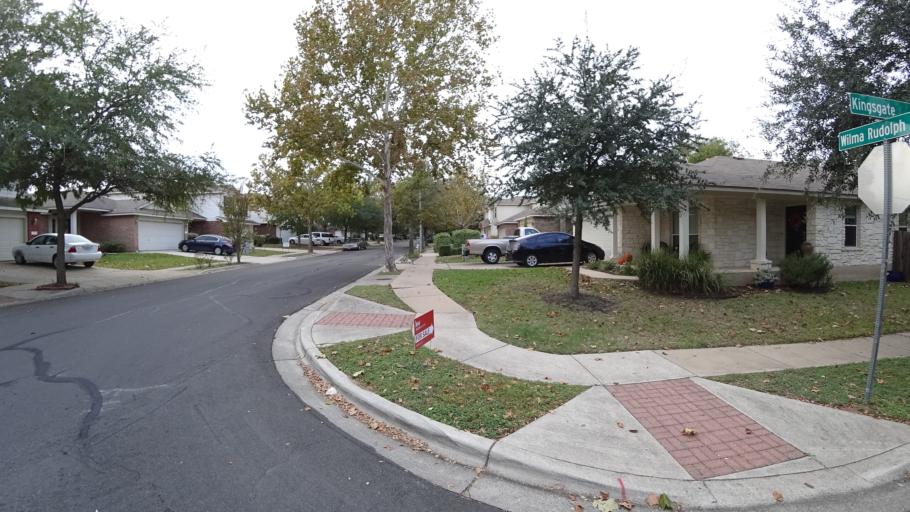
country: US
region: Texas
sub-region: Travis County
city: Manchaca
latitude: 30.1551
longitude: -97.8398
